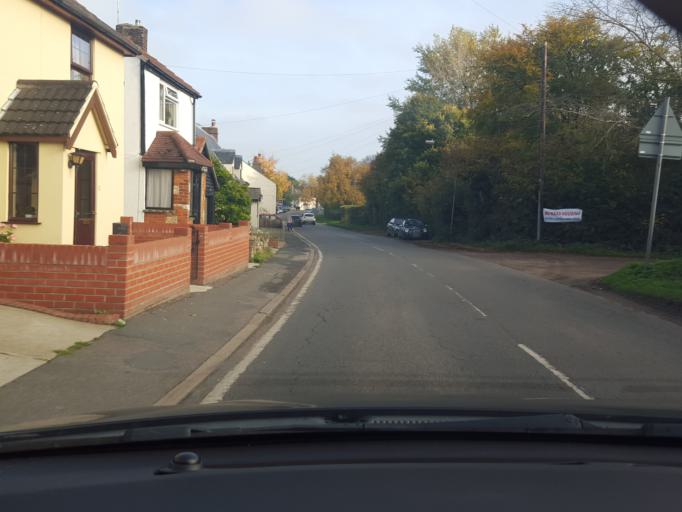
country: GB
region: England
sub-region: Essex
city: Frinton-on-Sea
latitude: 51.8540
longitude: 1.2195
